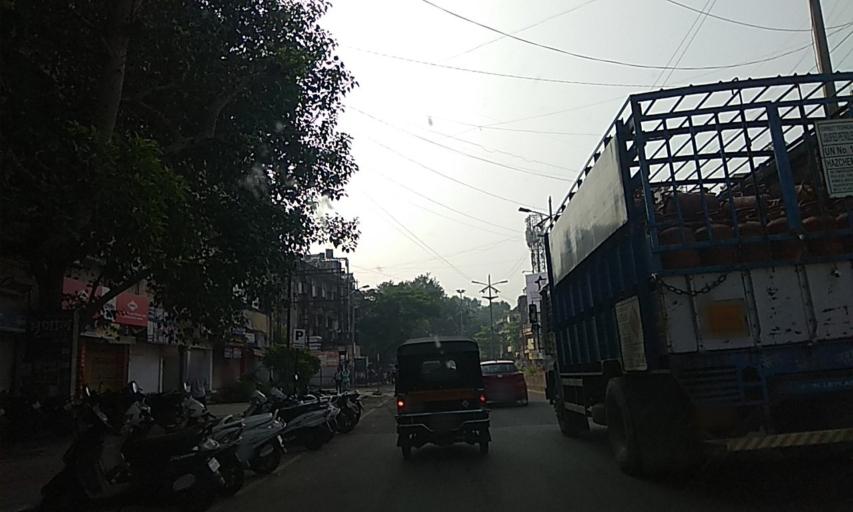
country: IN
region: Maharashtra
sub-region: Pune Division
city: Pune
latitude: 18.5102
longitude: 73.8434
